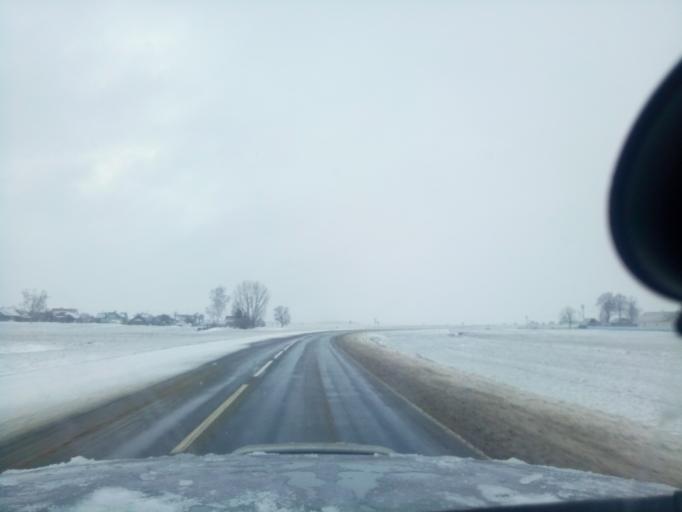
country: BY
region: Minsk
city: Haradzyeya
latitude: 53.3027
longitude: 26.5744
